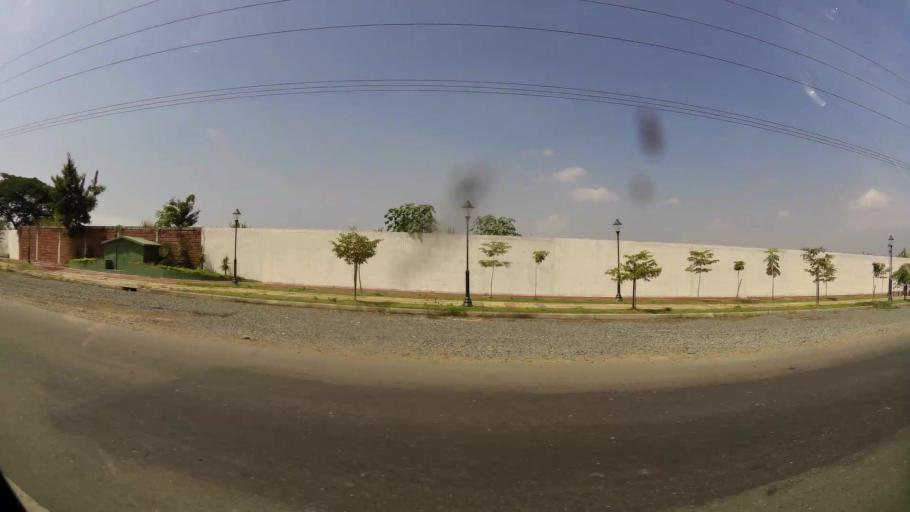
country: EC
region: Guayas
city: Eloy Alfaro
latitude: -2.0690
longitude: -79.8730
